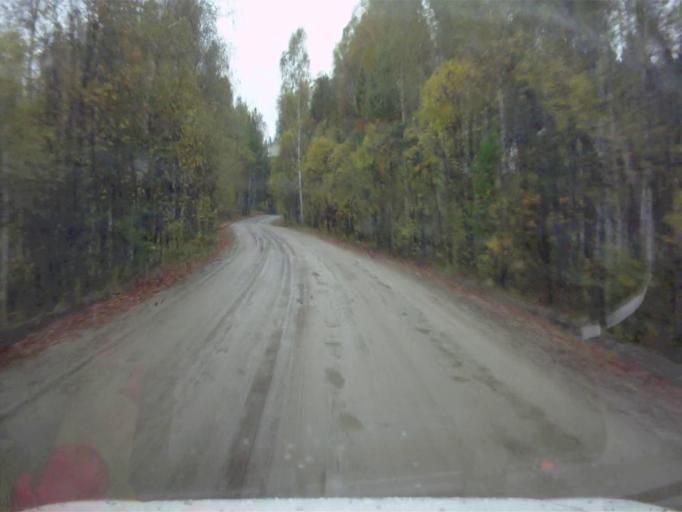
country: RU
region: Chelyabinsk
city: Kyshtym
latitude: 55.8284
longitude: 60.4871
